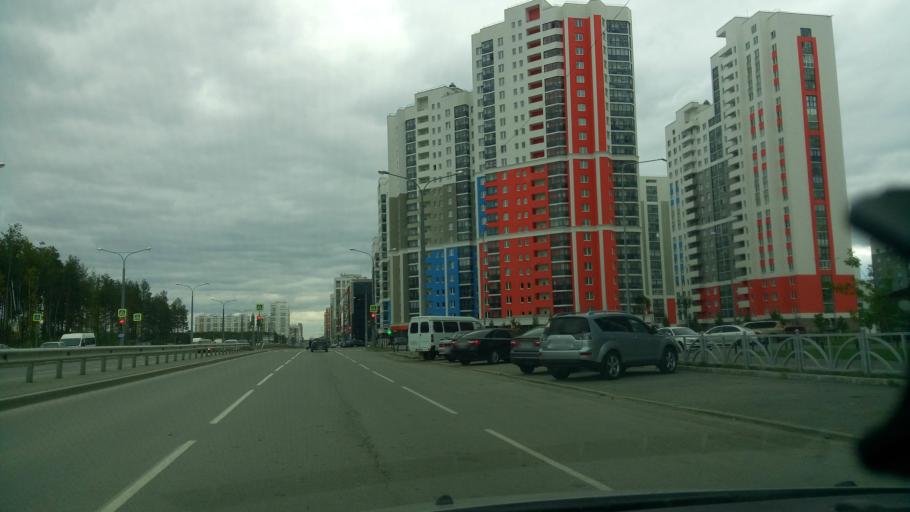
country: RU
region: Sverdlovsk
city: Shirokaya Rechka
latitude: 56.7962
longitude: 60.5158
